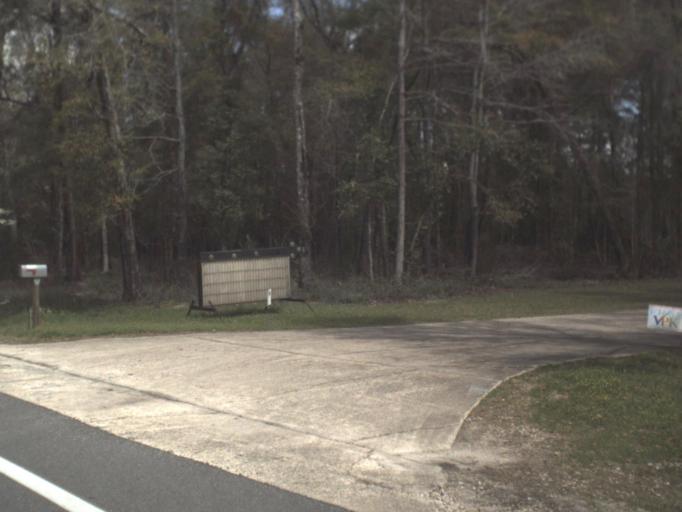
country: US
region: Florida
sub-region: Wakulla County
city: Crawfordville
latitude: 30.2295
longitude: -84.3624
